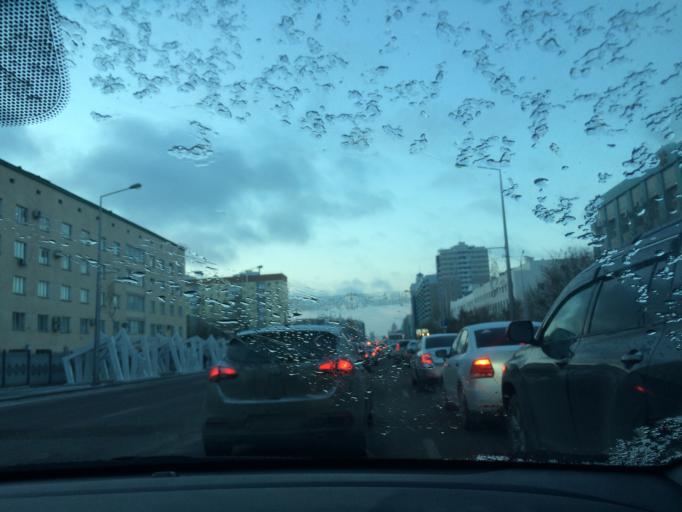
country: KZ
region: Astana Qalasy
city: Astana
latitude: 51.1717
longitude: 71.4071
